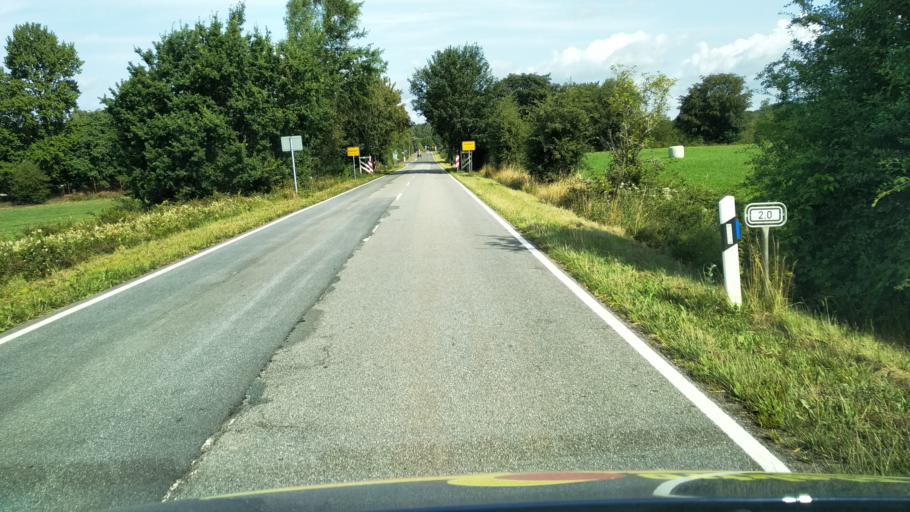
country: DE
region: Schleswig-Holstein
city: Brekendorf
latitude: 54.4173
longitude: 9.6321
